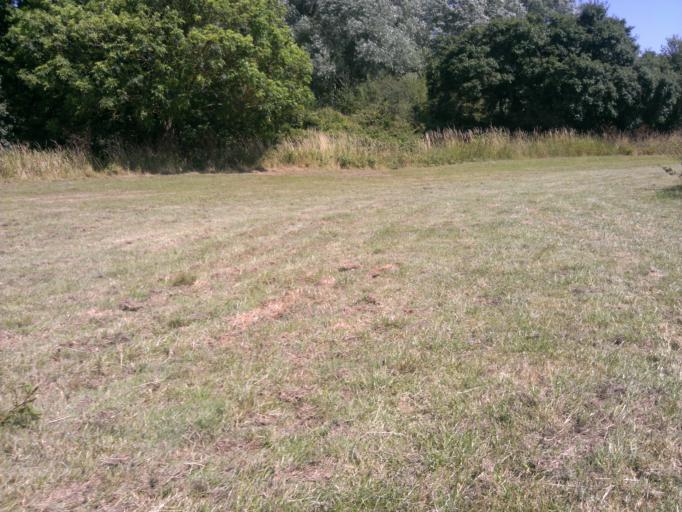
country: GB
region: England
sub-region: Essex
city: Clacton-on-Sea
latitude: 51.8063
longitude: 1.1646
